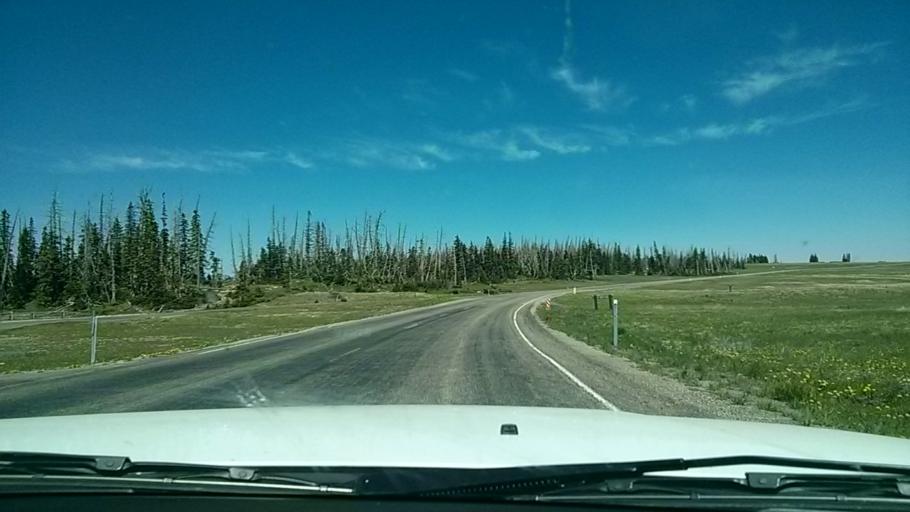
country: US
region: Utah
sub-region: Iron County
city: Parowan
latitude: 37.6569
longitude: -112.8319
